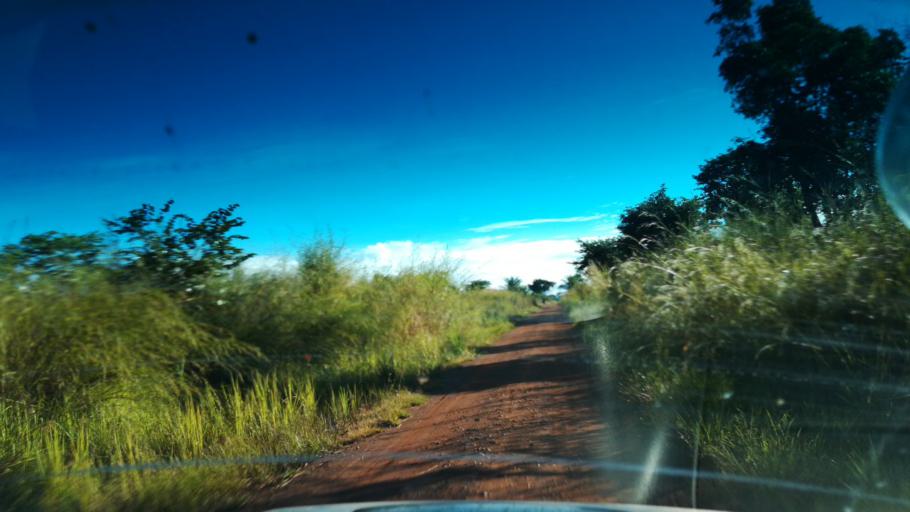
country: ZM
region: Northern
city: Kaputa
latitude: -8.3108
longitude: 29.0024
